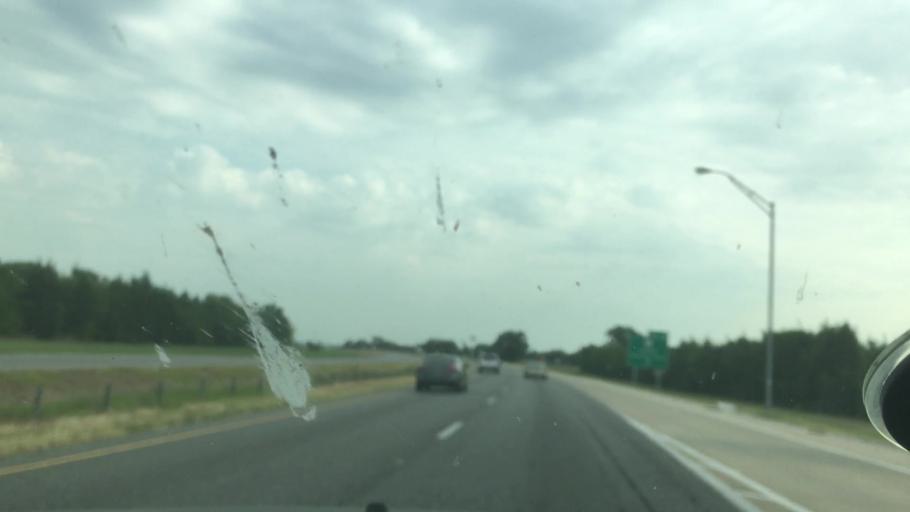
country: US
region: Oklahoma
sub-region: Bryan County
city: Colbert
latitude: 33.8471
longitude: -96.5123
